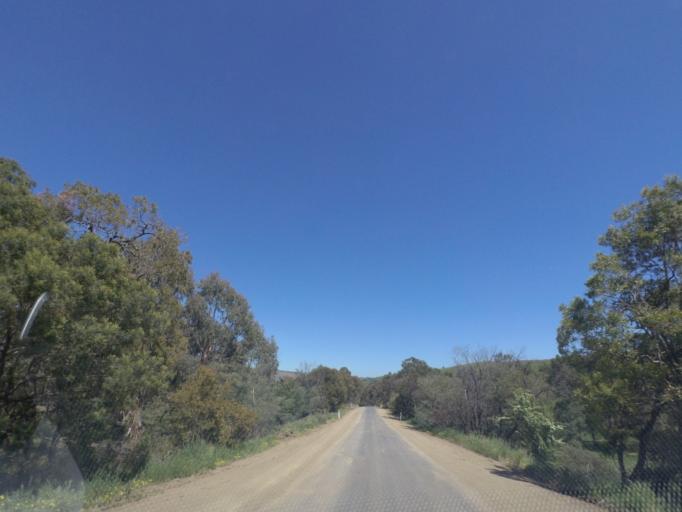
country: AU
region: Victoria
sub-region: Whittlesea
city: Whittlesea
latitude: -37.2839
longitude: 145.0028
